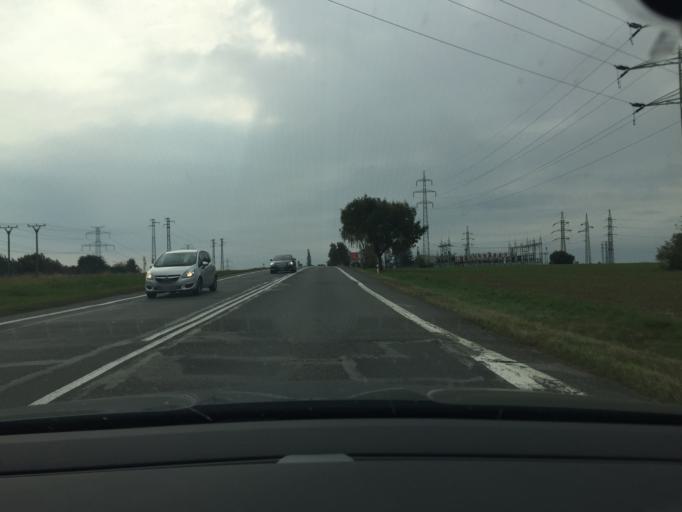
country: CZ
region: Jihocesky
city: Mirovice
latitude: 49.5178
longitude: 14.0727
